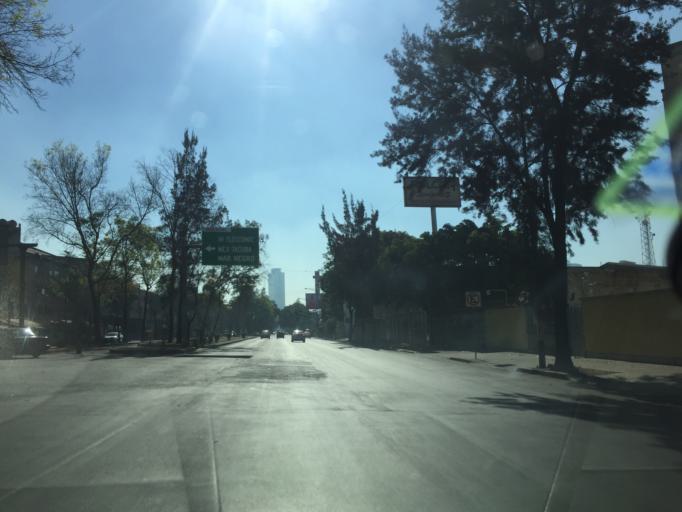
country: MX
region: Mexico City
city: Miguel Hidalgo
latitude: 19.4533
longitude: -99.1867
